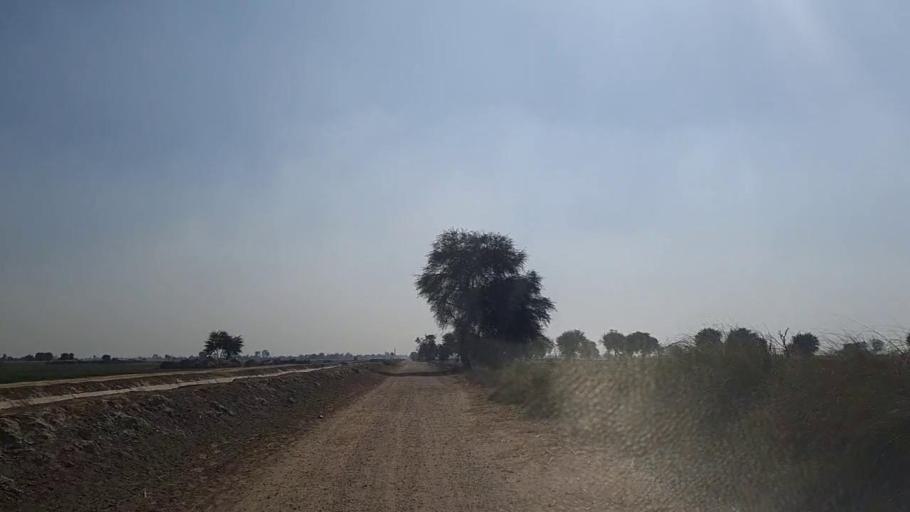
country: PK
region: Sindh
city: Shahpur Chakar
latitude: 26.2042
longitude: 68.5837
